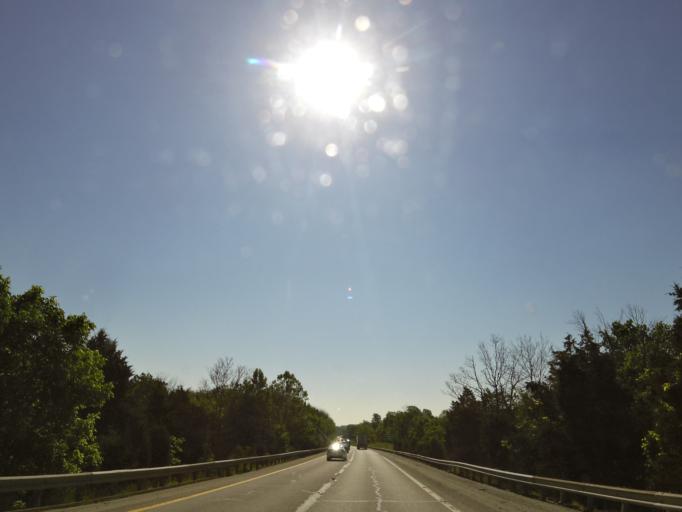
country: US
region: Kentucky
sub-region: Shelby County
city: Shelbyville
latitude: 38.1511
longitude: -85.0583
